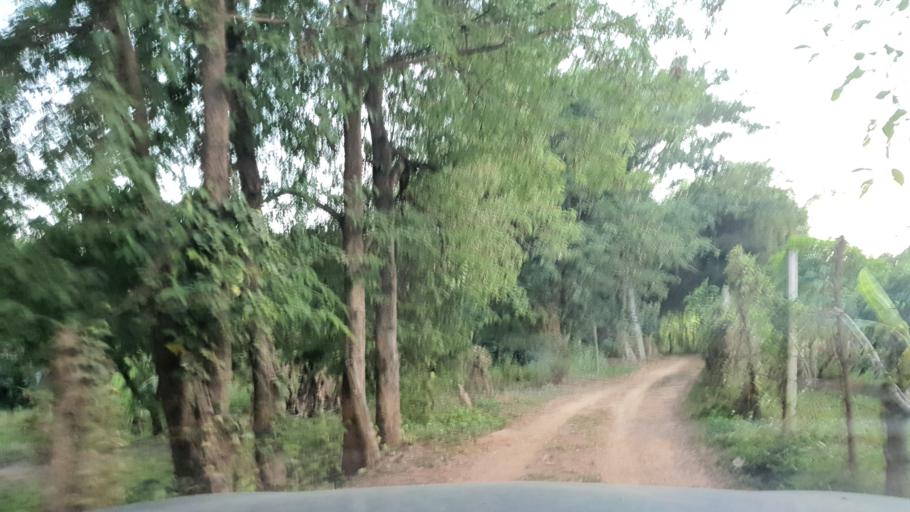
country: TH
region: Chiang Mai
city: Mae Wang
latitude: 18.6970
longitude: 98.8148
